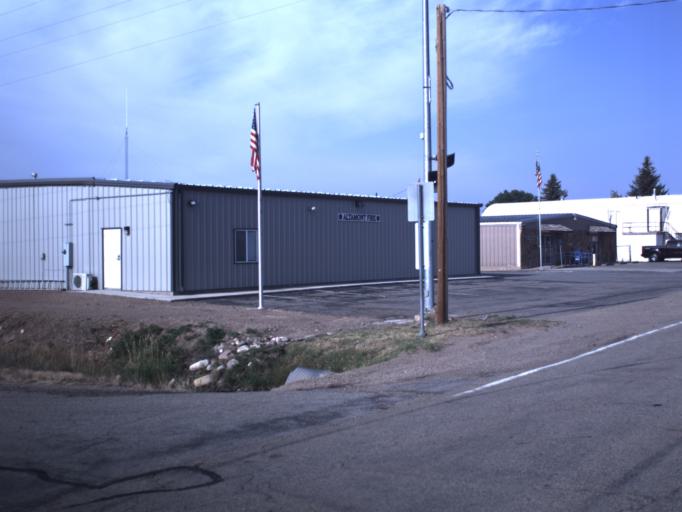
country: US
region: Utah
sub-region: Duchesne County
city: Duchesne
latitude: 40.3593
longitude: -110.2846
